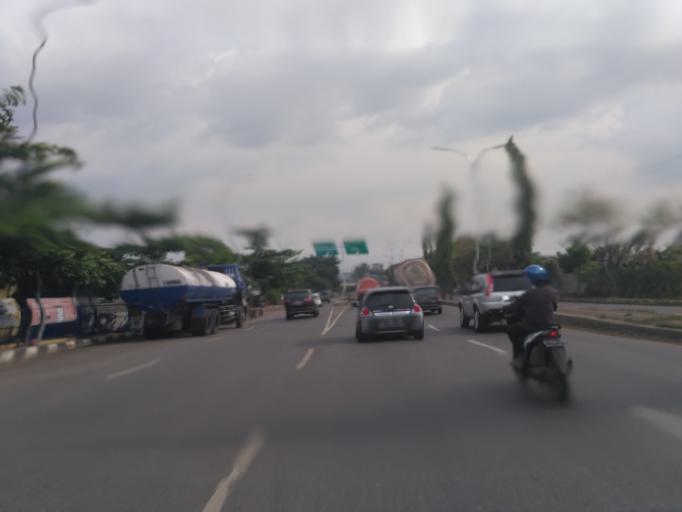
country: ID
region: Central Java
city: Semarang
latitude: -6.9818
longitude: 110.3866
